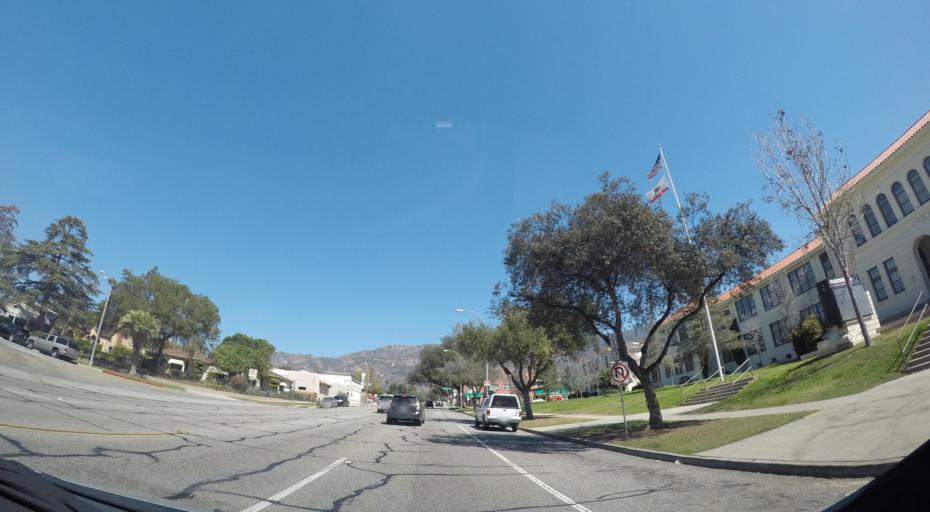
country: US
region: California
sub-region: Los Angeles County
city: East Pasadena
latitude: 34.1630
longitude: -118.1131
